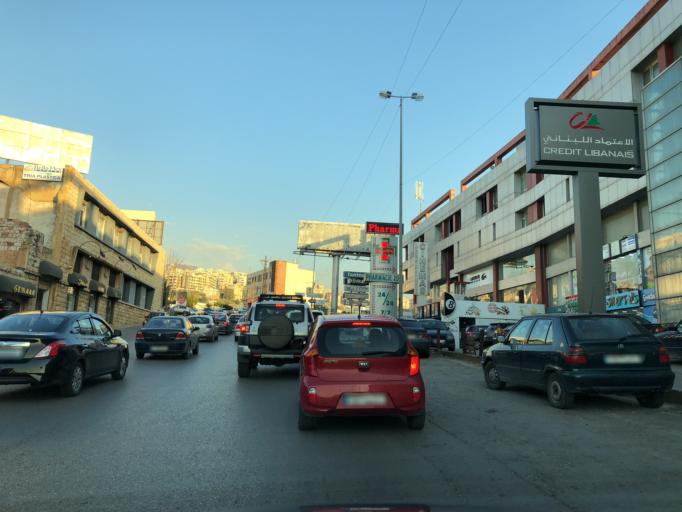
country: LB
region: Mont-Liban
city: Baabda
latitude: 33.8601
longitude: 35.5526
